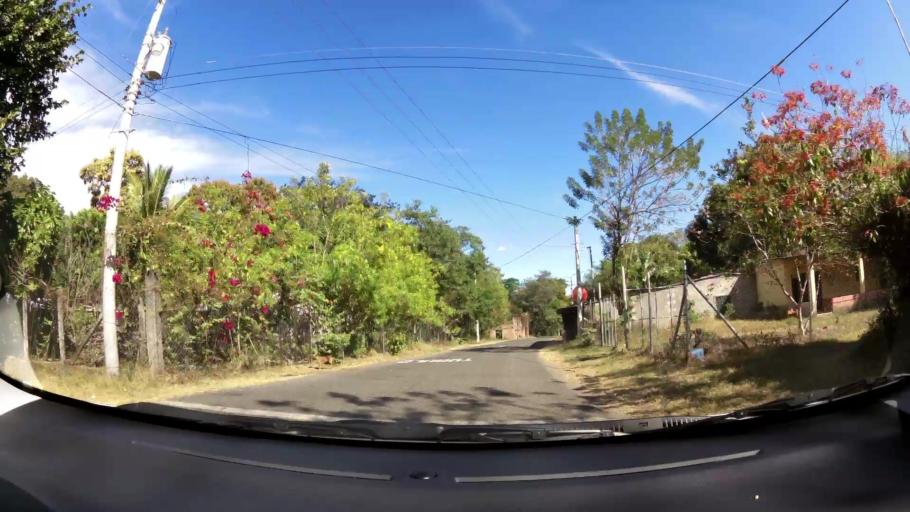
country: SV
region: Cuscatlan
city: Suchitoto
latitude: 13.9300
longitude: -89.0466
